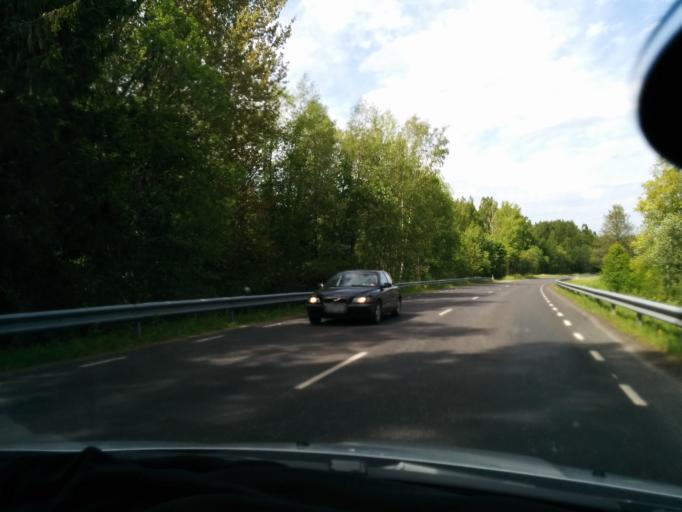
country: EE
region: Harju
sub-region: Loksa linn
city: Loksa
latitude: 59.5583
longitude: 25.7248
